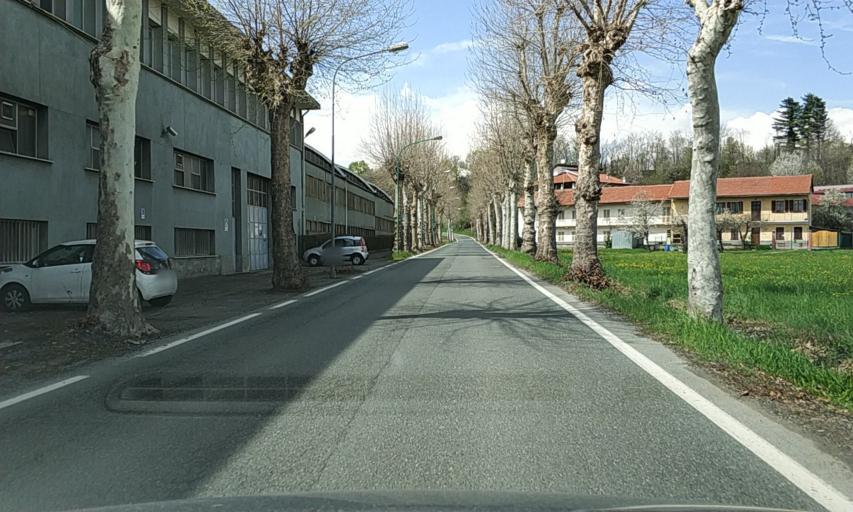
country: IT
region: Piedmont
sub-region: Provincia di Torino
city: San Carlo Canavese
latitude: 45.2445
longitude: 7.6005
